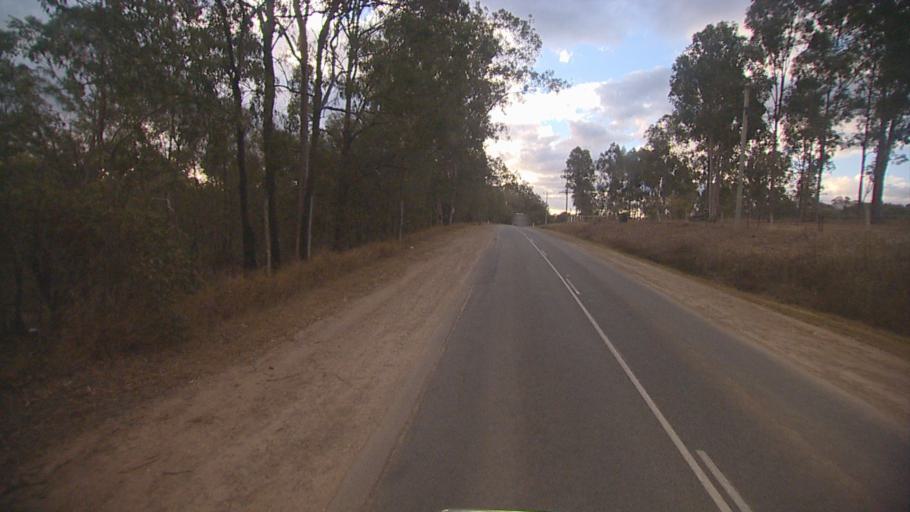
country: AU
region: Queensland
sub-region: Logan
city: Cedar Vale
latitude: -27.8577
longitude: 153.0543
